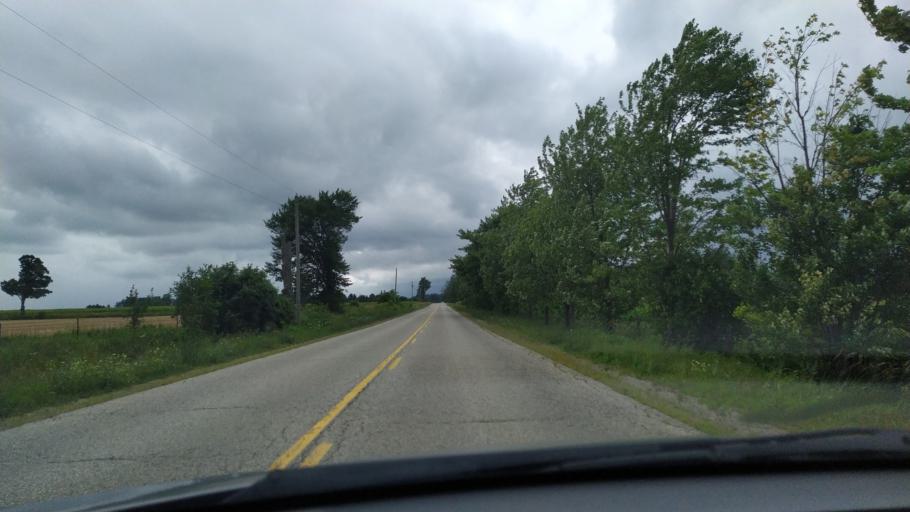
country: CA
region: Ontario
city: Kitchener
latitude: 43.3382
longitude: -80.6092
